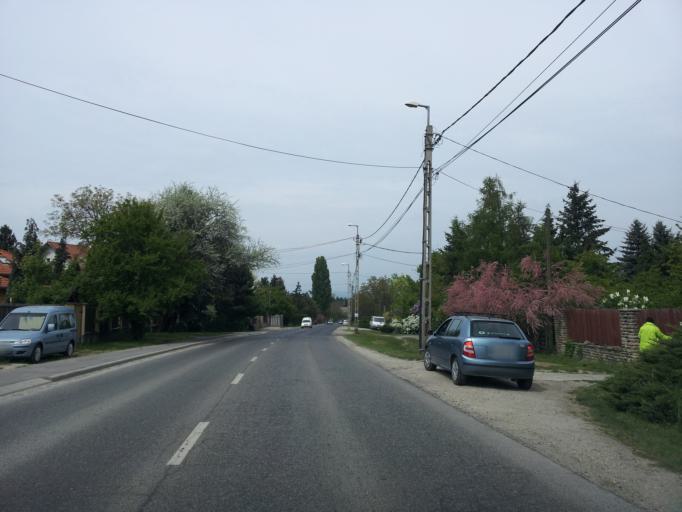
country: HU
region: Pest
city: Tahitotfalu
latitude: 47.7431
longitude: 19.0838
